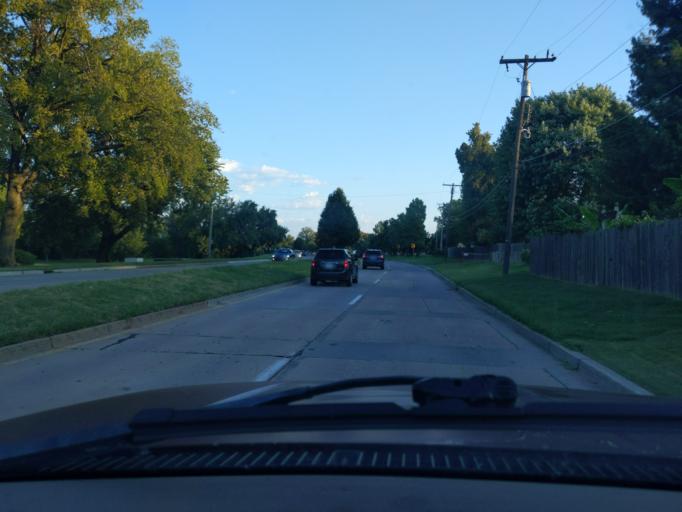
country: US
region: Oklahoma
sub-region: Tulsa County
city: Jenks
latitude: 36.0829
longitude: -95.9841
